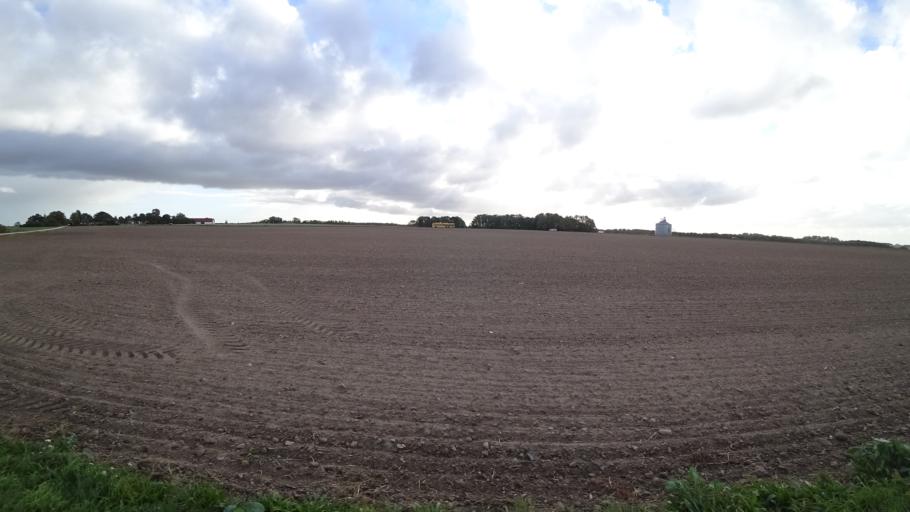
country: SE
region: Skane
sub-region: Kavlinge Kommun
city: Loddekopinge
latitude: 55.7784
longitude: 13.0597
